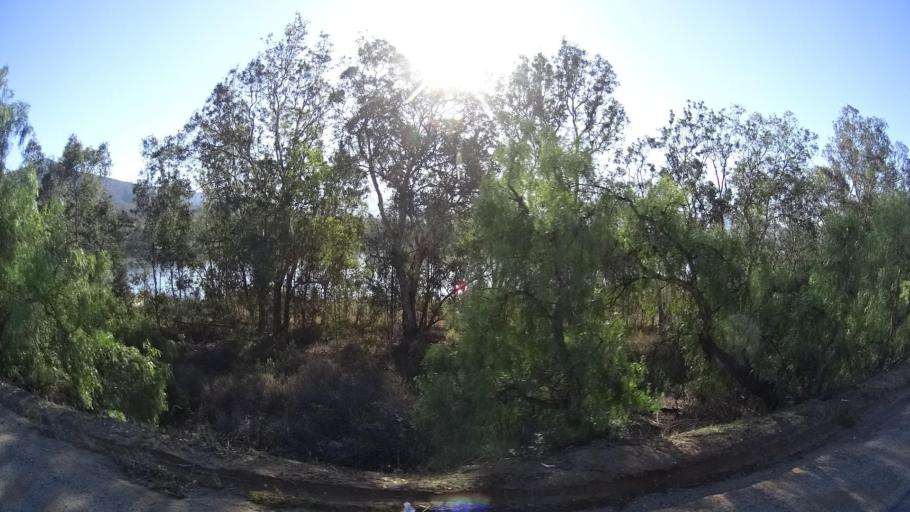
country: US
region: California
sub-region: San Diego County
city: La Presa
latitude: 32.6453
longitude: -116.9325
